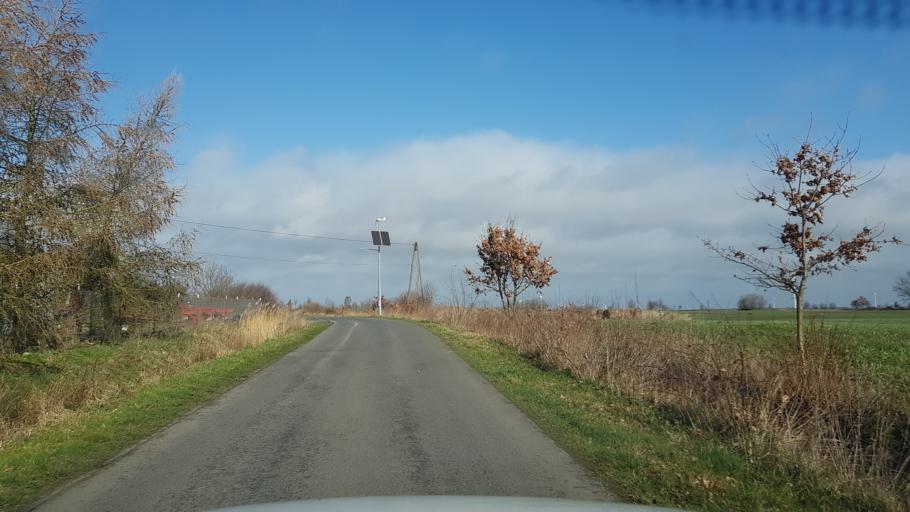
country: PL
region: West Pomeranian Voivodeship
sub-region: Powiat slawienski
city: Slawno
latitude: 54.4926
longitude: 16.6492
